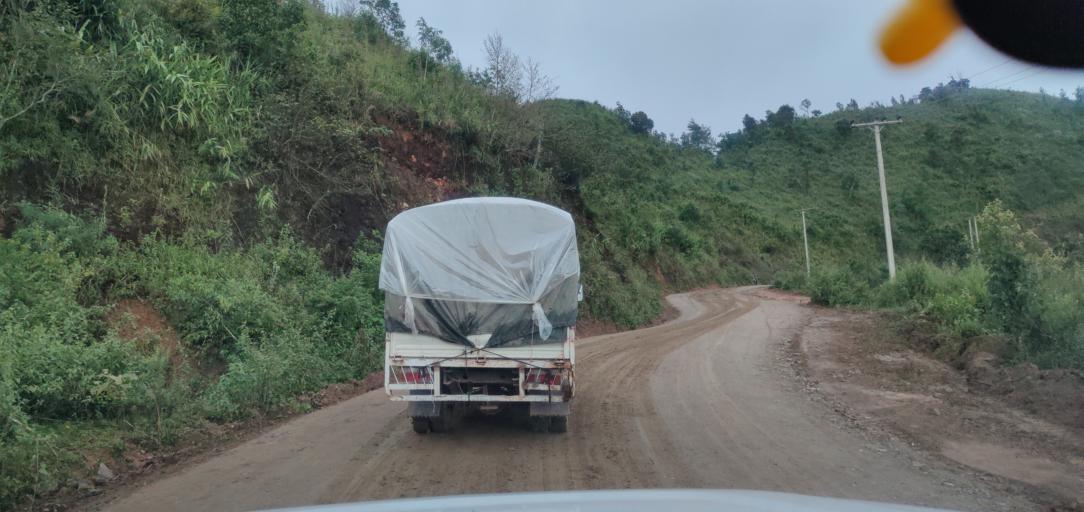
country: LA
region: Phongsali
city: Phongsali
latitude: 21.4238
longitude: 102.1723
